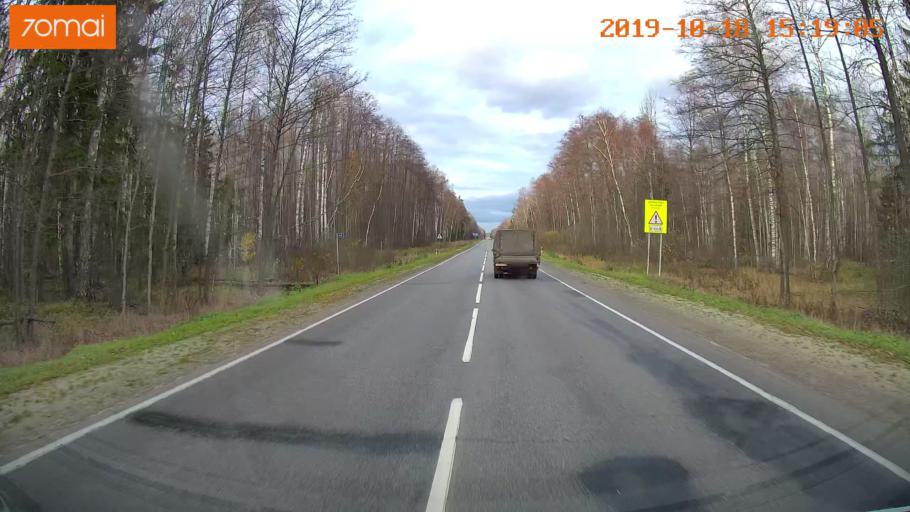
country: RU
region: Vladimir
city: Anopino
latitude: 55.6678
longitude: 40.7350
